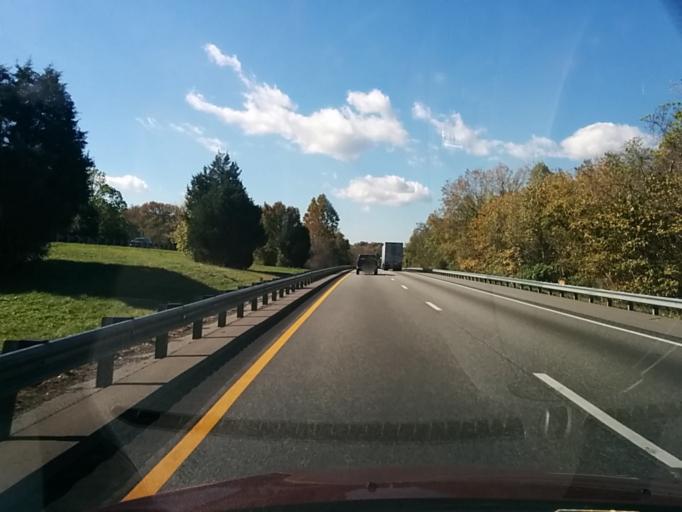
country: US
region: Virginia
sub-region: Botetourt County
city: Fincastle
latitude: 37.4828
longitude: -79.7793
